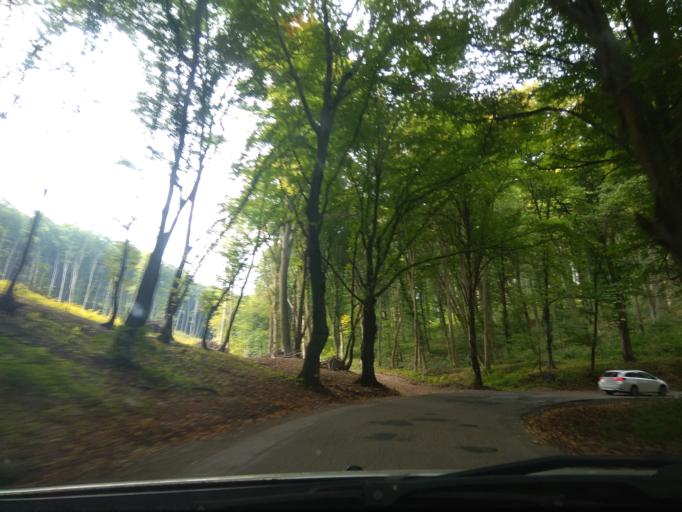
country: HU
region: Borsod-Abauj-Zemplen
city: Miskolc
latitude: 48.0637
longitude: 20.6818
